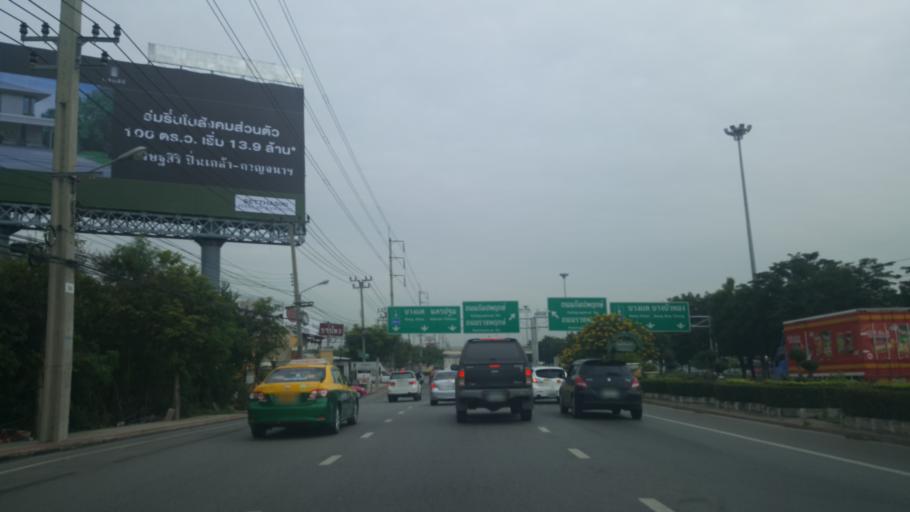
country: TH
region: Bangkok
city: Bang Khae
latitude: 13.6762
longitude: 100.4062
